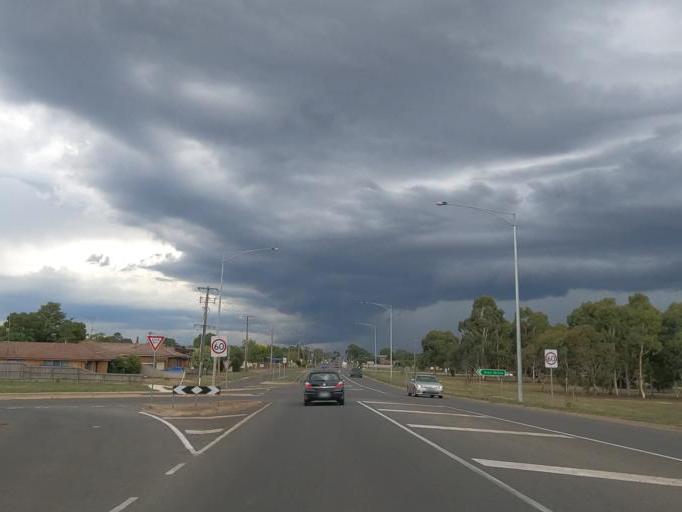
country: AU
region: Victoria
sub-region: Ballarat North
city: Lake Wendouree
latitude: -37.5192
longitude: 143.8260
